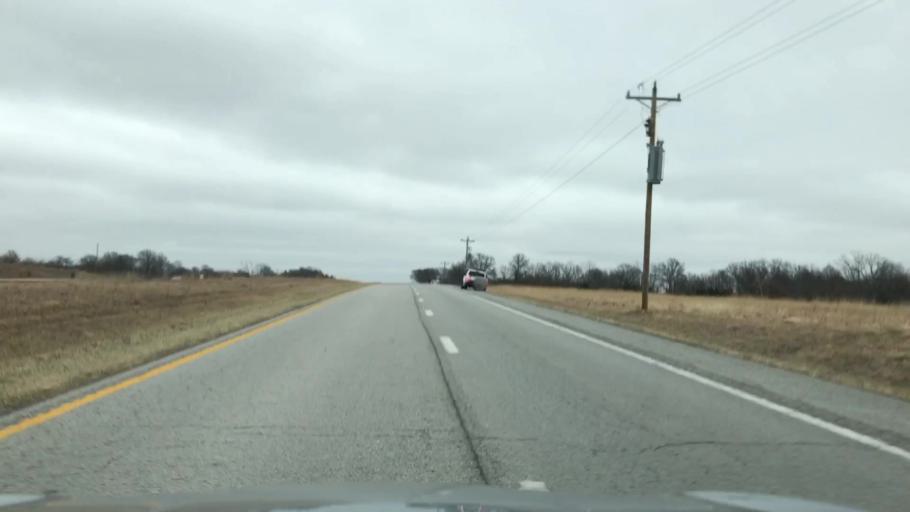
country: US
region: Missouri
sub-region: Linn County
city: Linneus
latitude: 39.7782
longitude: -93.1813
